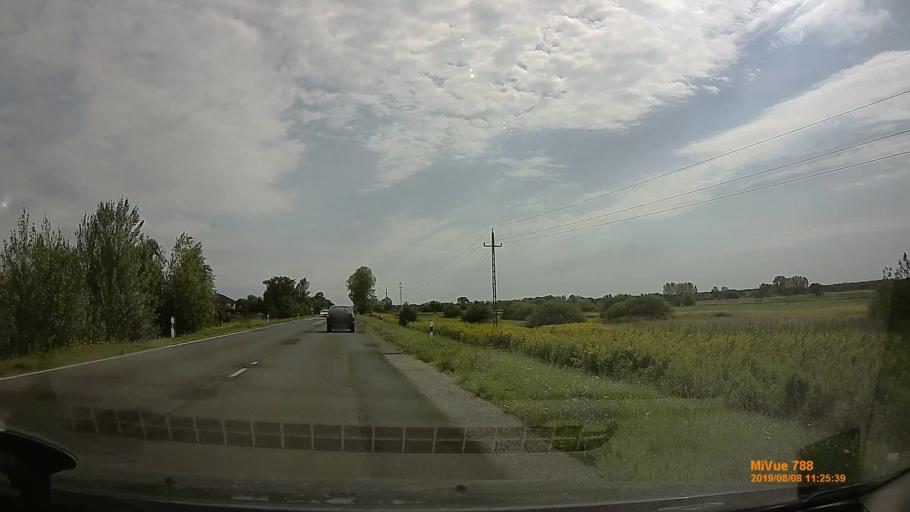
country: HU
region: Somogy
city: Kethely
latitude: 46.6994
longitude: 17.4294
